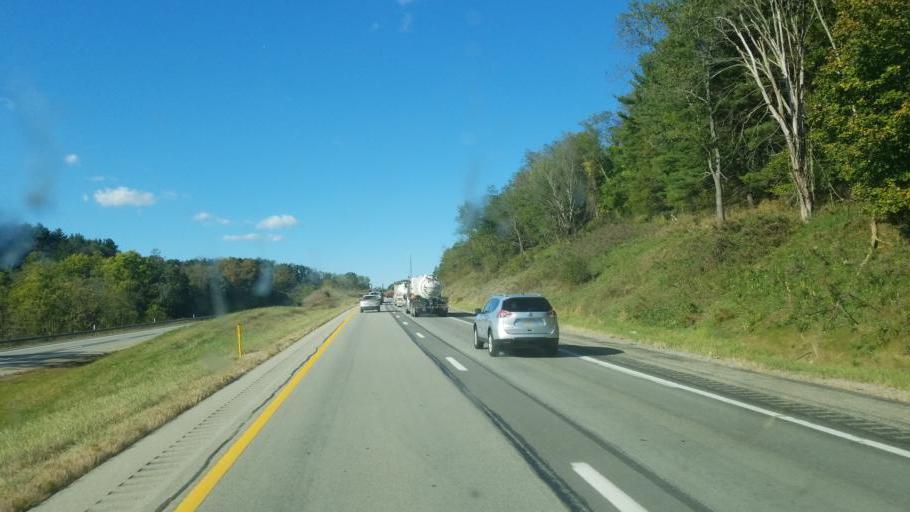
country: US
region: Pennsylvania
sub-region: Washington County
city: East Washington
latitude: 40.0577
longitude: -80.1859
